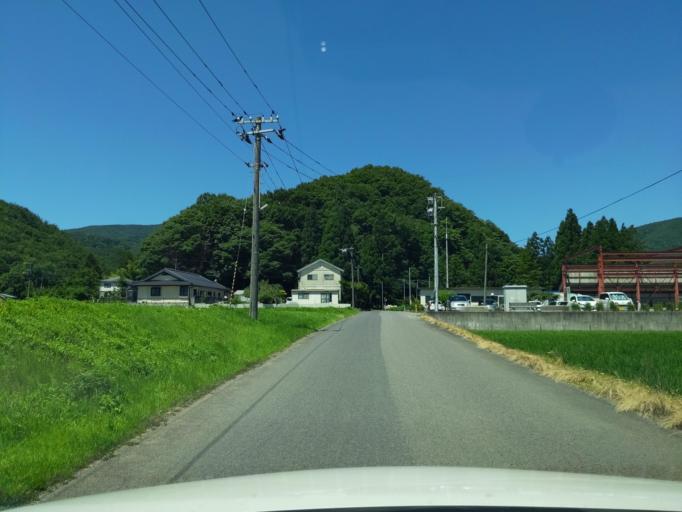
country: JP
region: Fukushima
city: Koriyama
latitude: 37.3896
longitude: 140.2410
